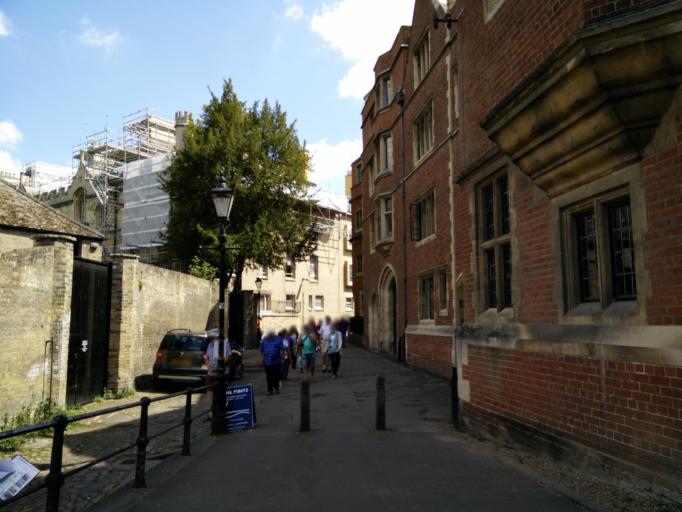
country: GB
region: England
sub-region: Cambridgeshire
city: Cambridge
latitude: 52.2060
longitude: 0.1143
